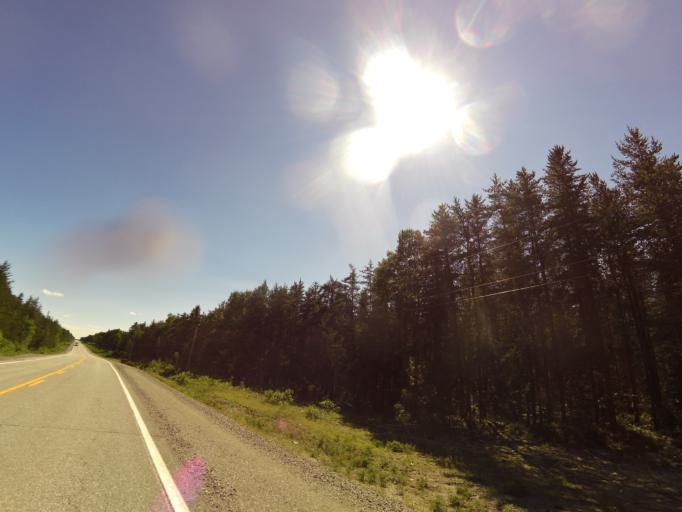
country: CA
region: Quebec
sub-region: Abitibi-Temiscamingue
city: Senneterre
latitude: 48.1375
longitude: -77.3749
